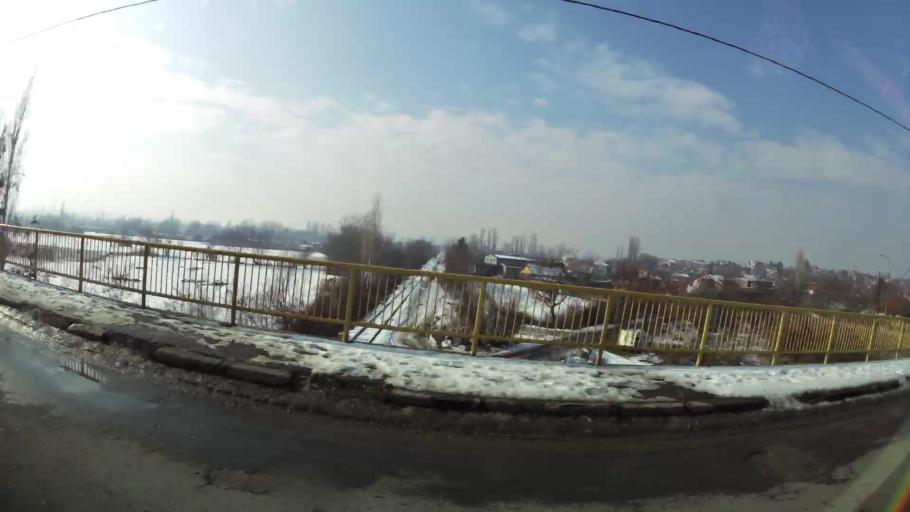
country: MK
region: Suto Orizari
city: Suto Orizare
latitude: 42.0246
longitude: 21.3844
